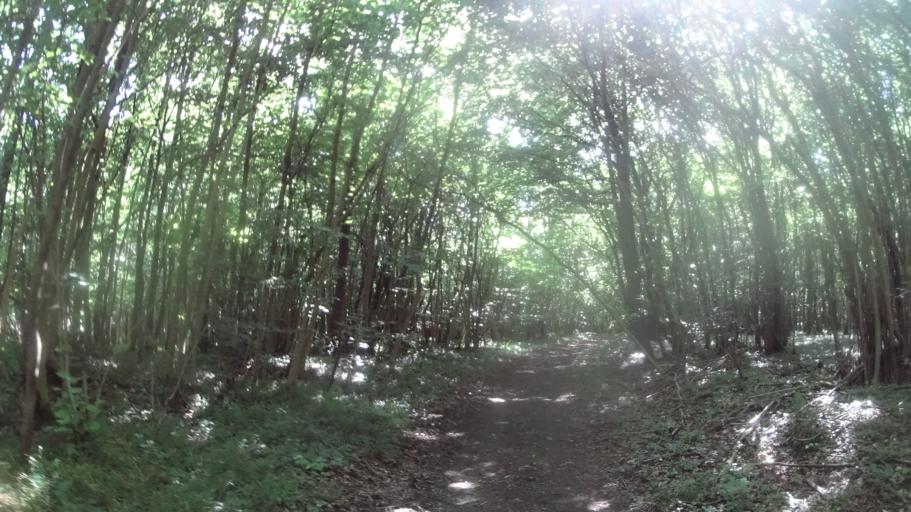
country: DE
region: Lower Saxony
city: Elbe
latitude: 52.1088
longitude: 10.3066
